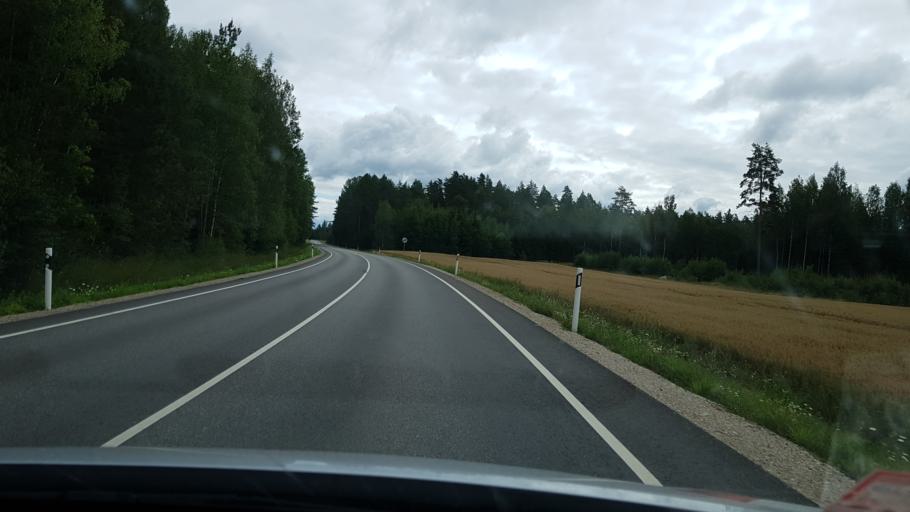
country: EE
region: Polvamaa
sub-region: Polva linn
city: Polva
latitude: 58.0038
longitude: 27.2112
